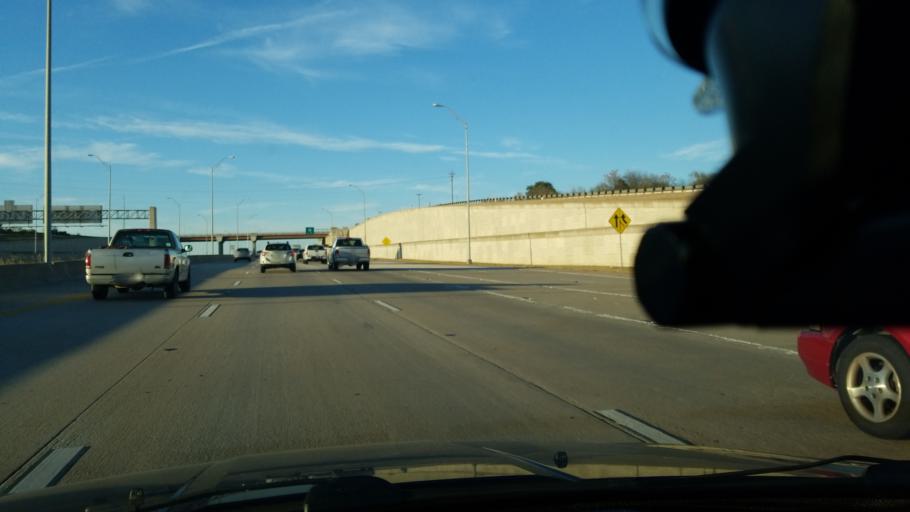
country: US
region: Texas
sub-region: Travis County
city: Wells Branch
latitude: 30.4573
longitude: -97.6980
